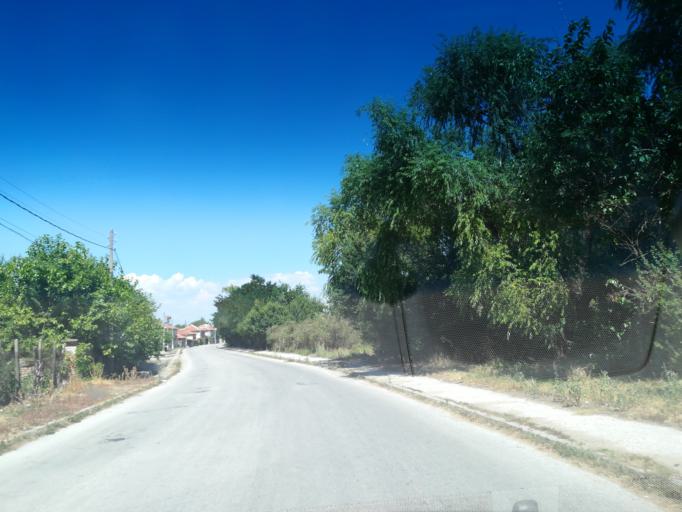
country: BG
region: Plovdiv
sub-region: Obshtina Sadovo
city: Sadovo
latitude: 42.0228
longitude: 25.1019
